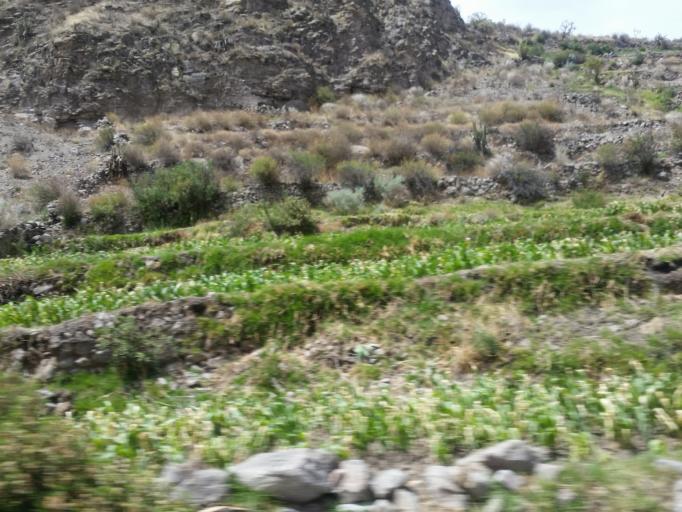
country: PE
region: Arequipa
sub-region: Provincia de Caylloma
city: Achoma
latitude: -15.6555
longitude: -71.7269
